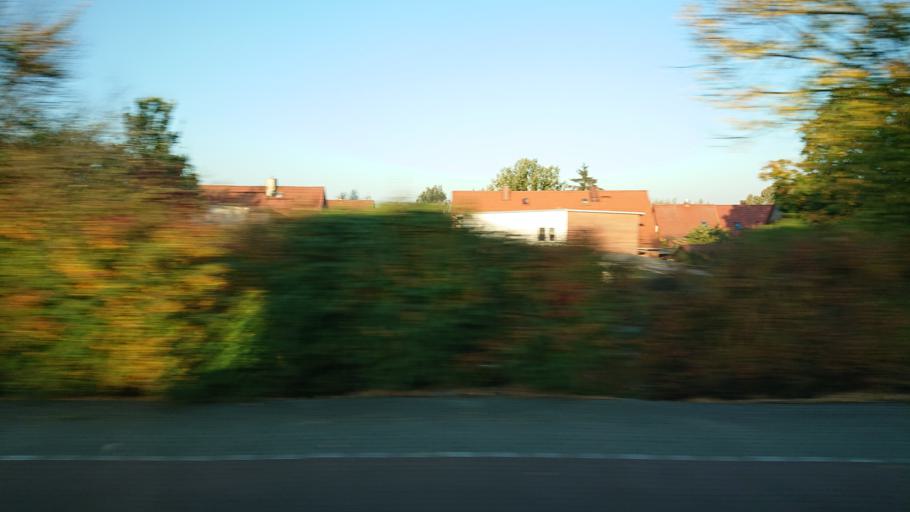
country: DE
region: Mecklenburg-Vorpommern
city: Neubrandenburg
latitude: 53.5763
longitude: 13.2694
